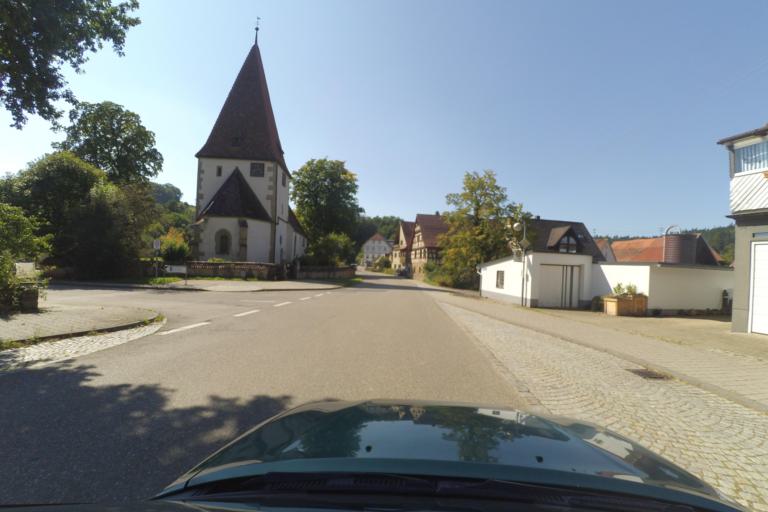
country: DE
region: Baden-Wuerttemberg
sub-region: Regierungsbezirk Stuttgart
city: Taferrot
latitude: 48.8498
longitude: 9.8386
